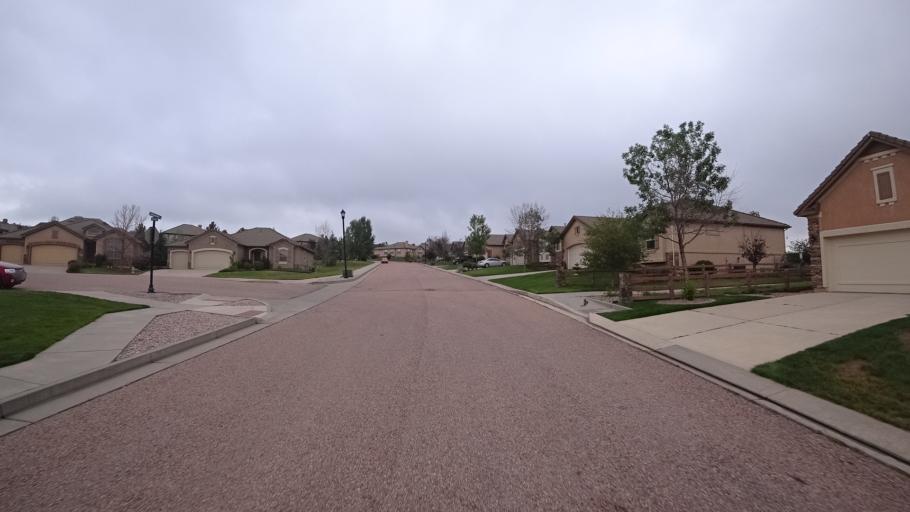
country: US
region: Colorado
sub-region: El Paso County
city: Gleneagle
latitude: 39.0323
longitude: -104.7777
